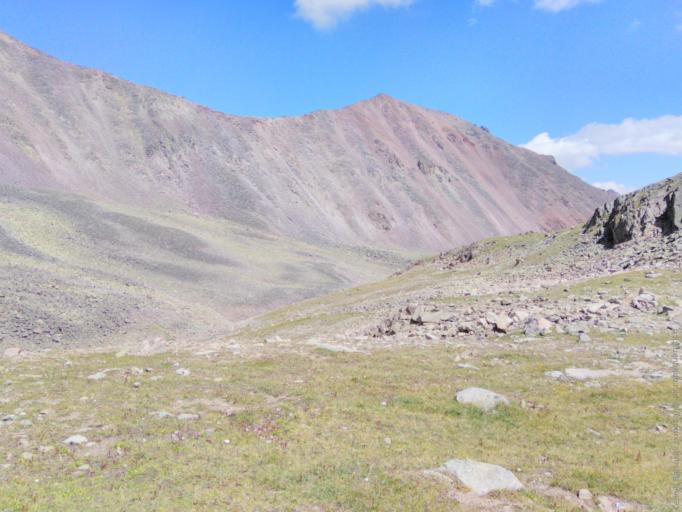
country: RU
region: Kabardino-Balkariya
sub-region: El'brusskiy Rayon
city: El'brus
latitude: 43.3280
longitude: 42.6760
